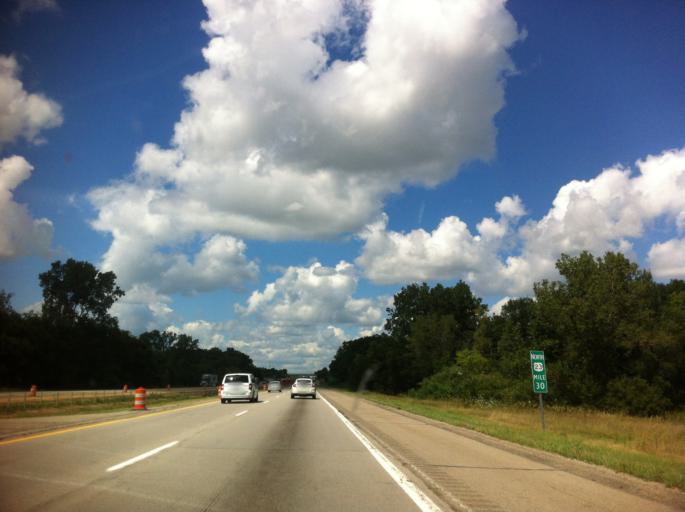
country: US
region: Michigan
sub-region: Washtenaw County
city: Milan
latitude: 42.1467
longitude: -83.6835
